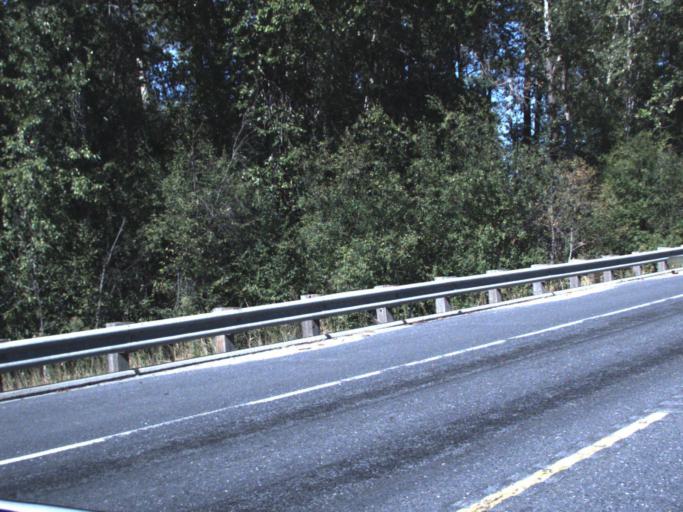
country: US
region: Washington
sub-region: Stevens County
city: Chewelah
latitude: 48.3320
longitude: -117.8279
